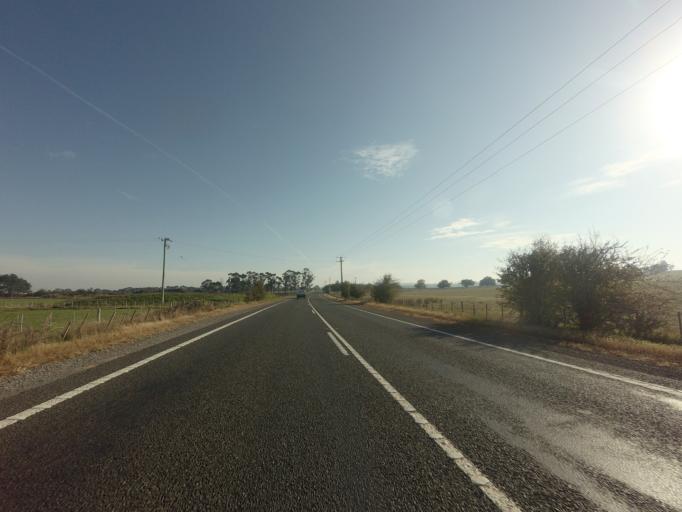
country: AU
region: Tasmania
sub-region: Northern Midlands
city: Longford
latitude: -41.5546
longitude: 147.0627
